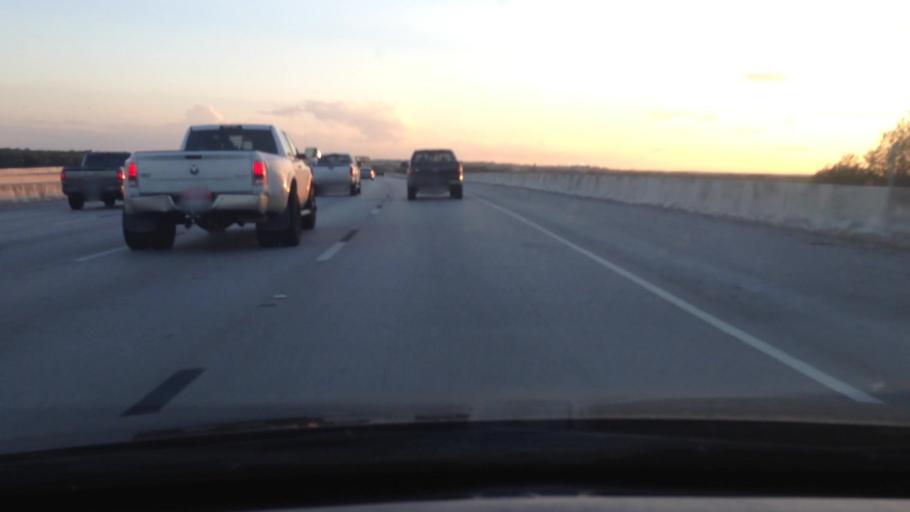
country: US
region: Texas
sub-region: Tarrant County
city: Lake Worth
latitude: 32.7955
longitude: -97.4520
